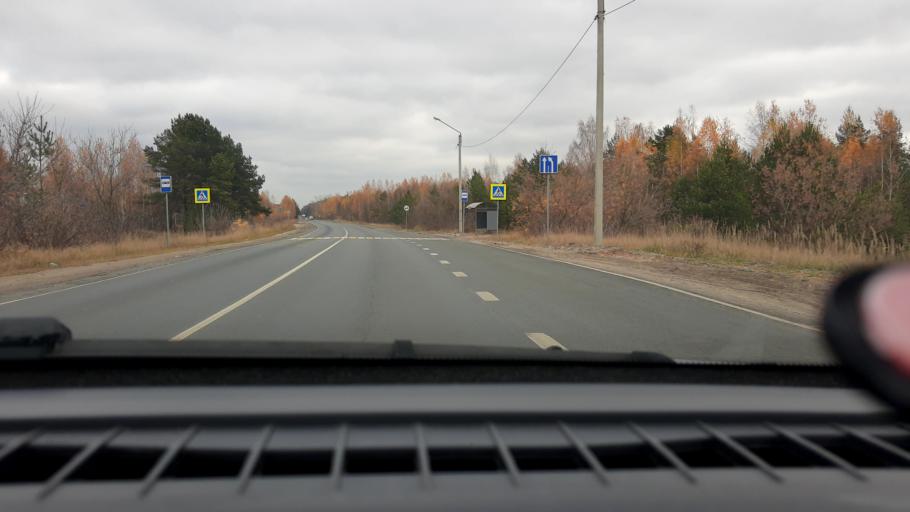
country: RU
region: Nizjnij Novgorod
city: Babino
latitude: 56.2599
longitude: 43.6619
